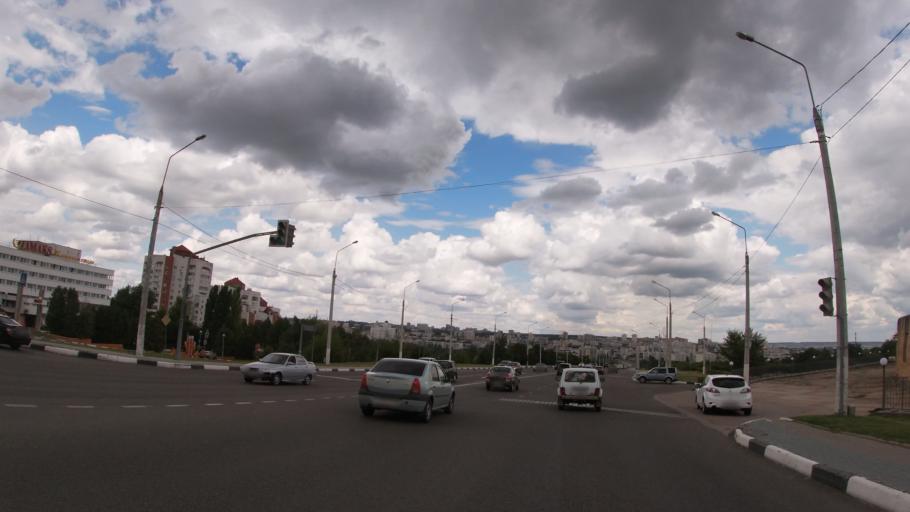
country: RU
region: Belgorod
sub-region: Belgorodskiy Rayon
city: Belgorod
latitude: 50.5808
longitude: 36.5831
